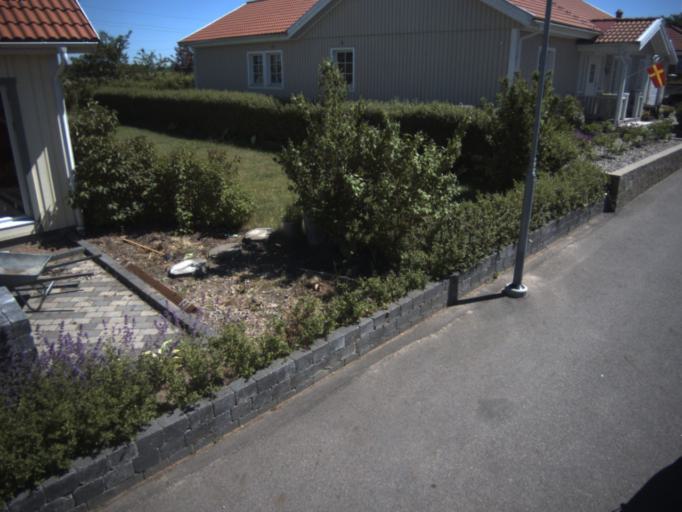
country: SE
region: Skane
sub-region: Helsingborg
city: Morarp
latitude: 56.0578
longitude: 12.8848
